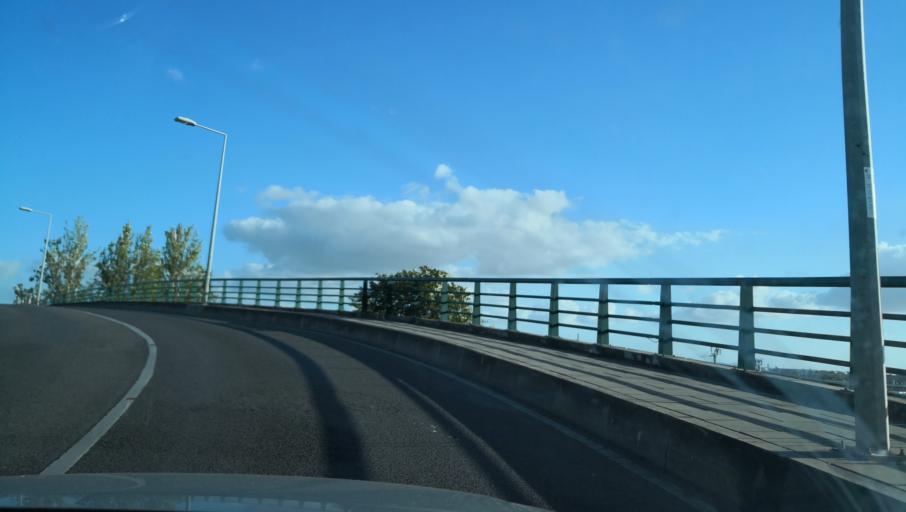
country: PT
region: Setubal
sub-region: Barreiro
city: Barreiro
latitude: 38.6559
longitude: -9.0786
